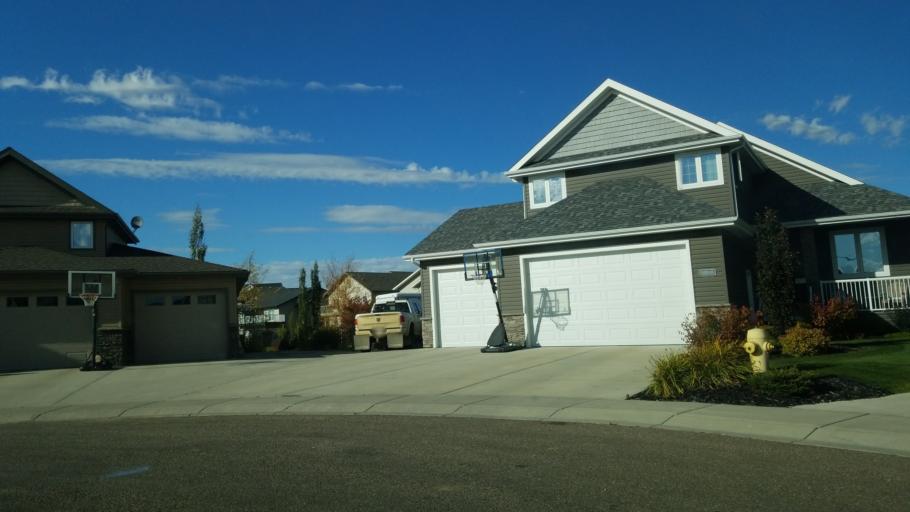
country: CA
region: Saskatchewan
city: Lloydminster
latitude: 53.2531
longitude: -110.0154
